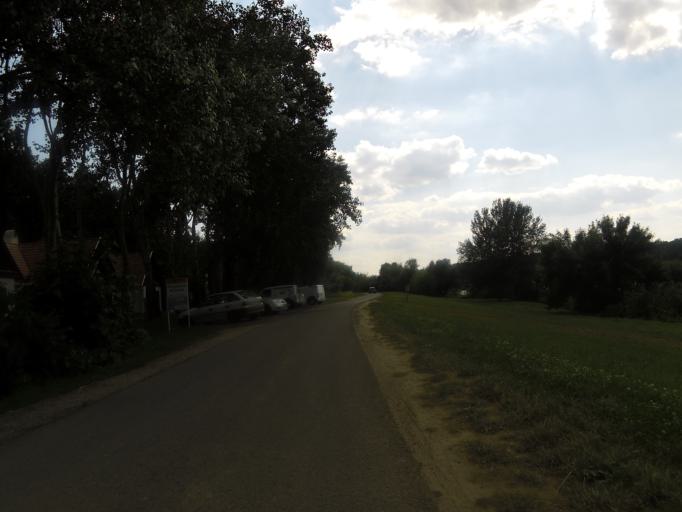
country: HU
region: Jasz-Nagykun-Szolnok
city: Tiszafured
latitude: 47.6202
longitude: 20.7286
